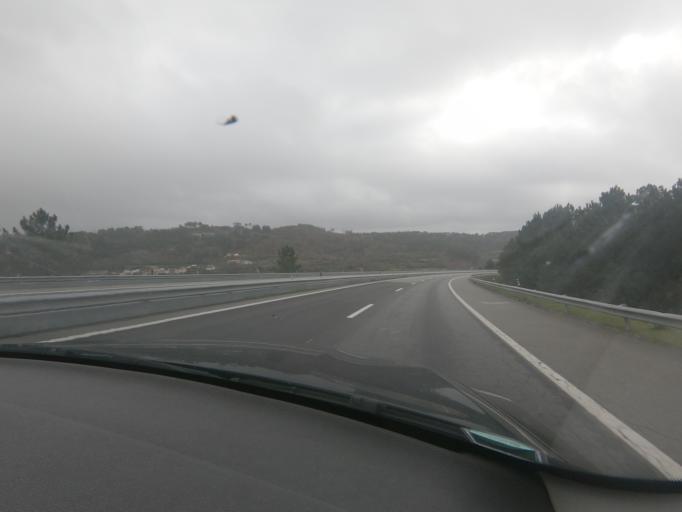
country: PT
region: Viseu
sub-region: Castro Daire
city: Castro Daire
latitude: 40.9094
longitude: -7.9065
